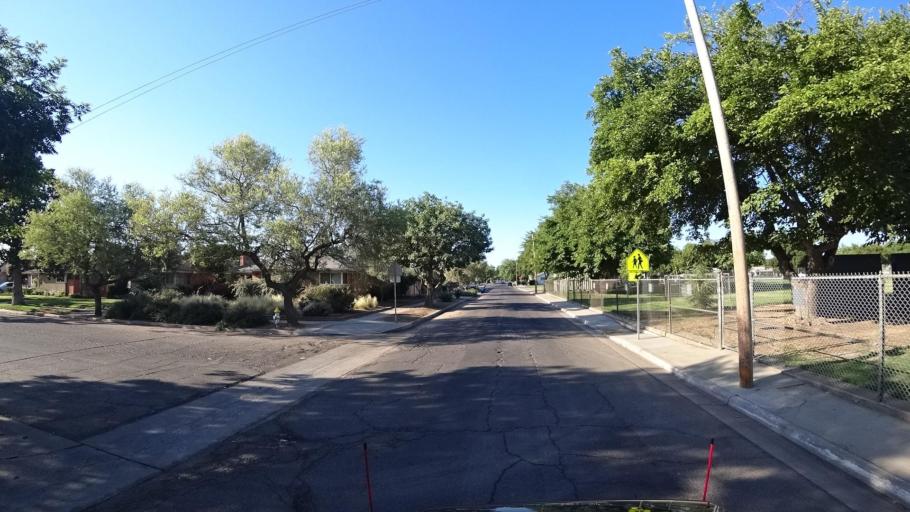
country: US
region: California
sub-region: Fresno County
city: Fresno
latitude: 36.7748
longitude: -119.8289
